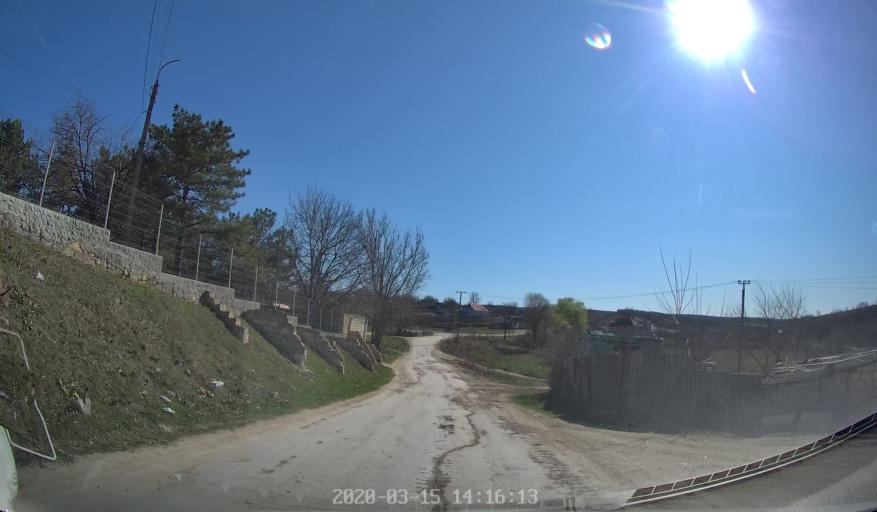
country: MD
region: Orhei
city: Orhei
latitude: 47.3110
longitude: 28.9320
